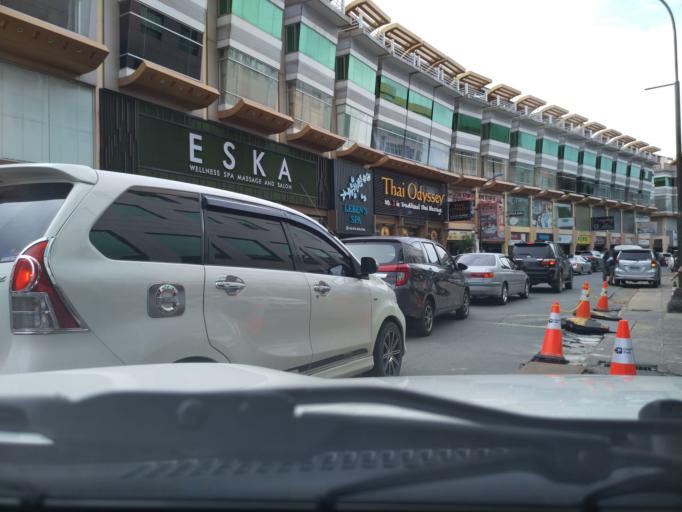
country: SG
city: Singapore
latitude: 1.1459
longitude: 104.0120
